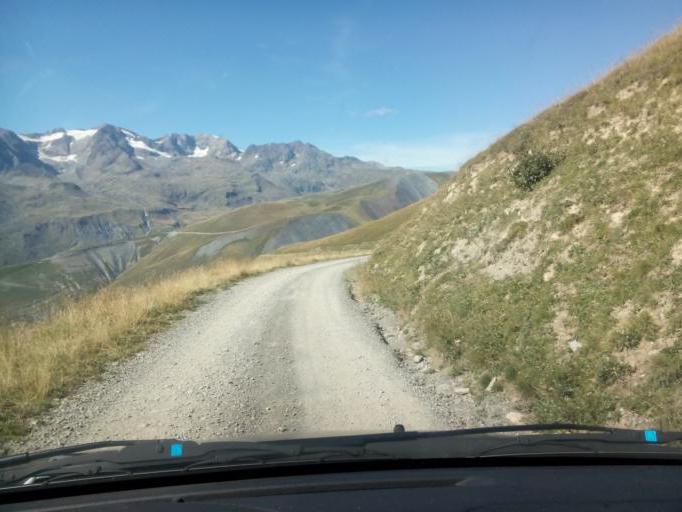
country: FR
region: Rhone-Alpes
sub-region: Departement de l'Isere
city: Mont-de-Lans
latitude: 45.0690
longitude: 6.2006
